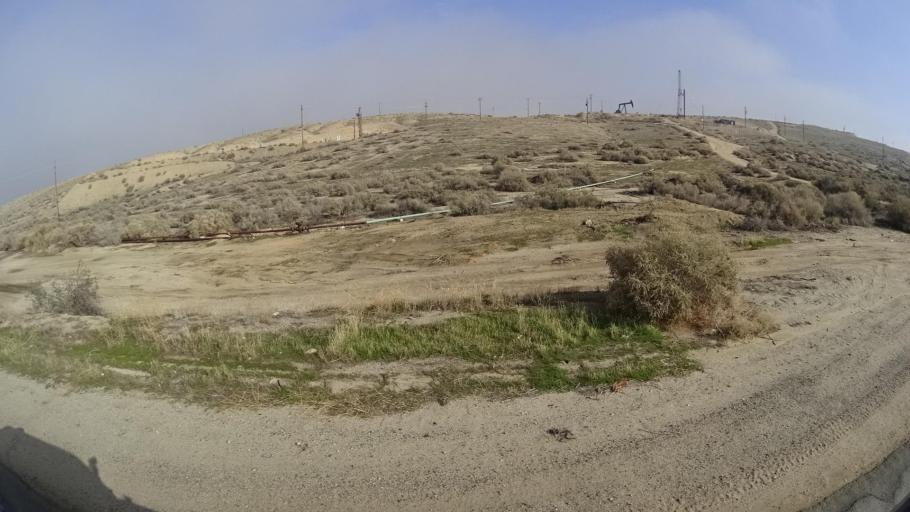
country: US
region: California
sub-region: Kern County
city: Ford City
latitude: 35.1706
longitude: -119.4229
